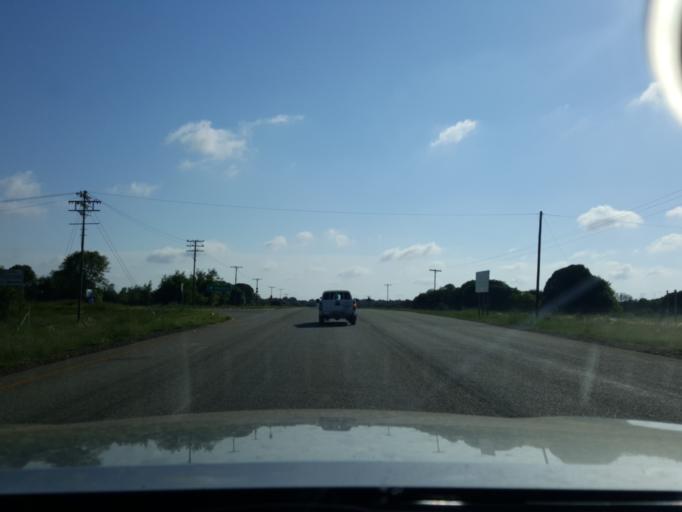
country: ZA
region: North-West
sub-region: Ngaka Modiri Molema District Municipality
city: Zeerust
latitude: -25.7517
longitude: 25.9691
